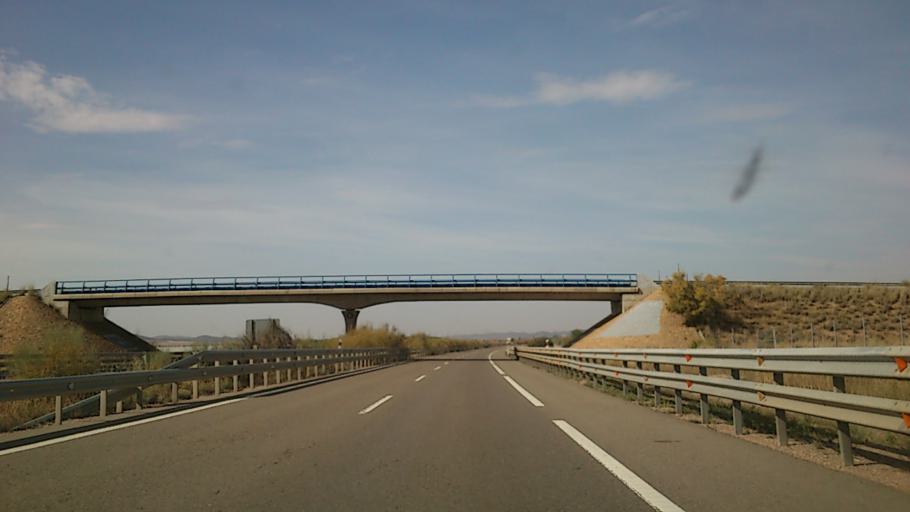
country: ES
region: Aragon
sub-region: Provincia de Teruel
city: Fuentes Claras
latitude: 40.8517
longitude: -1.3097
